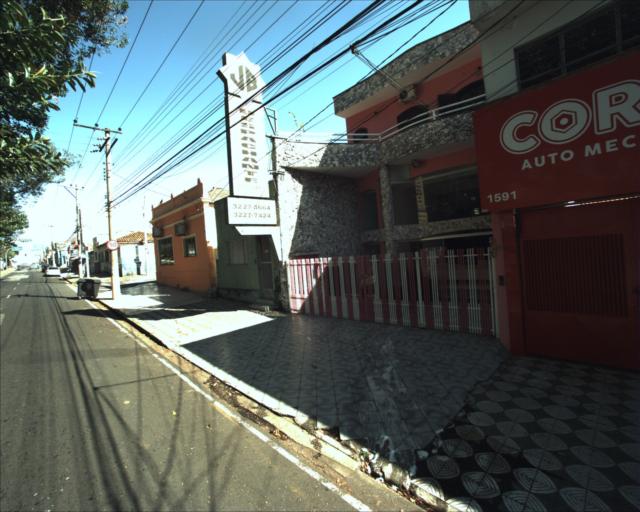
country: BR
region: Sao Paulo
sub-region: Sorocaba
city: Sorocaba
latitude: -23.4949
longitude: -47.4378
